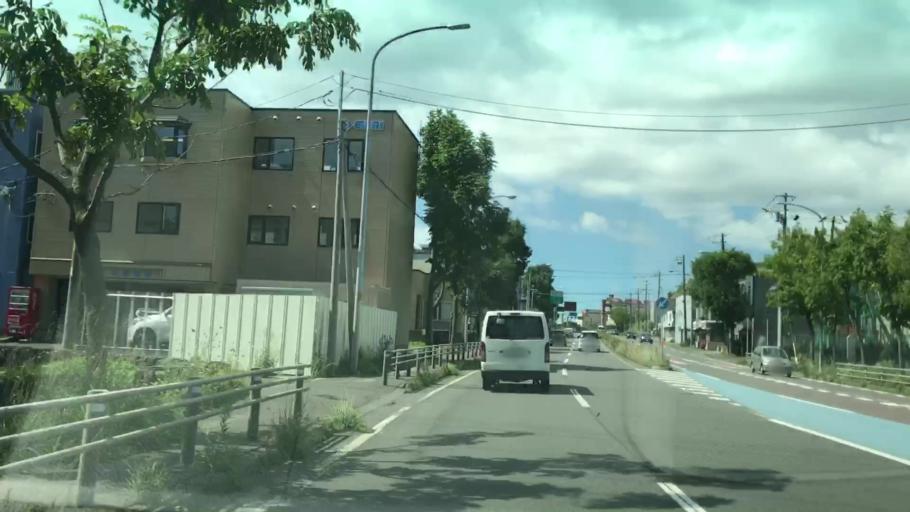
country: JP
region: Hokkaido
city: Muroran
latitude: 42.3372
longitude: 141.0221
